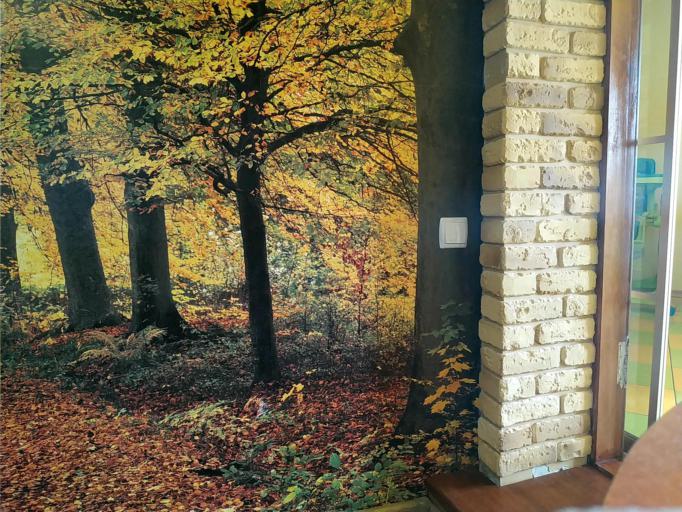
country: RU
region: Smolensk
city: Katyn'
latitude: 54.9381
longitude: 31.7285
